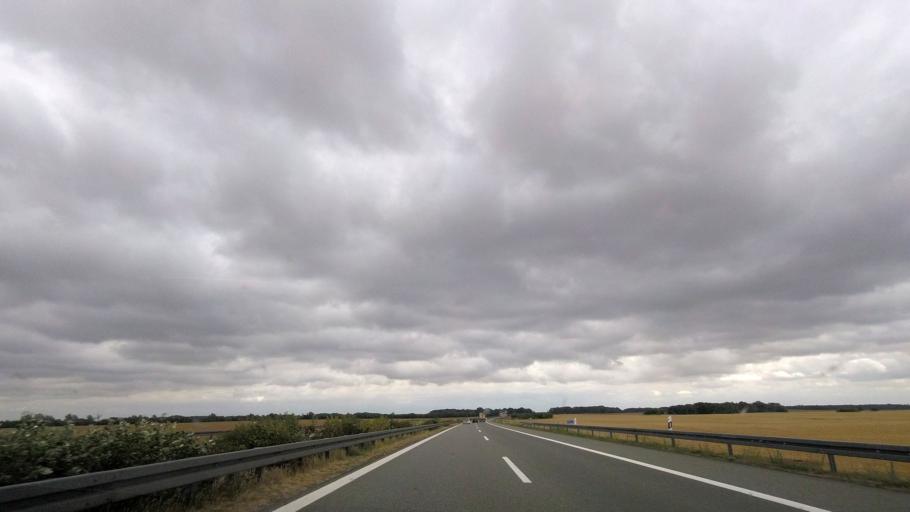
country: DE
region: Mecklenburg-Vorpommern
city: Jarmen
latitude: 53.9902
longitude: 13.3374
